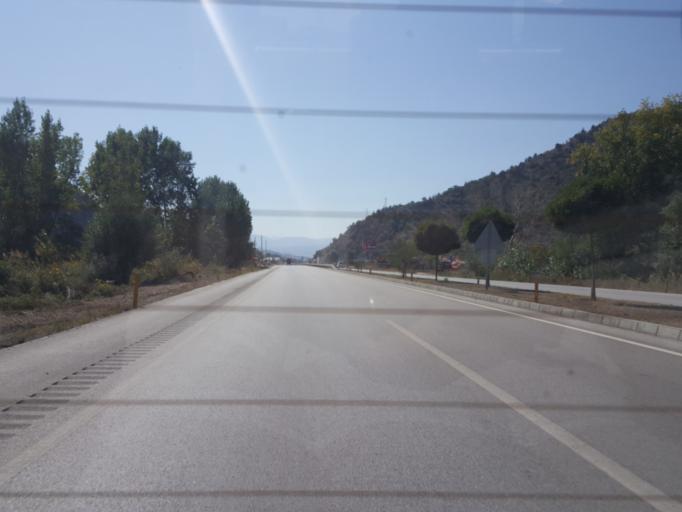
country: TR
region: Corum
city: Osmancik
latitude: 40.9746
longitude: 34.9132
